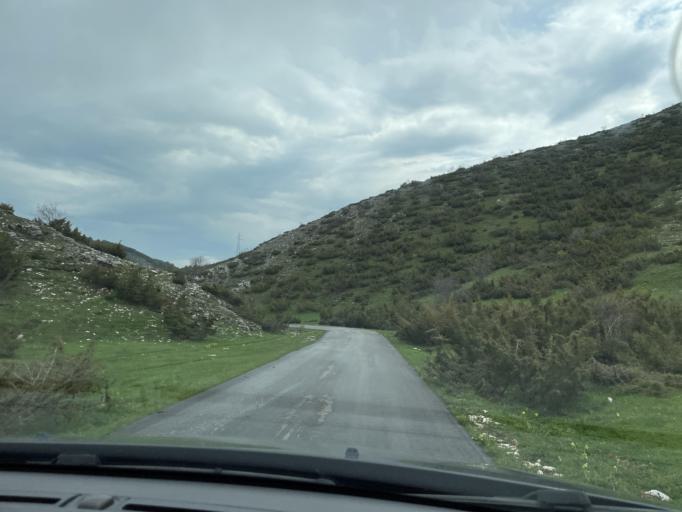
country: MK
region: Opstina Rostusa
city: Rostusha
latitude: 41.6113
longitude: 20.6801
